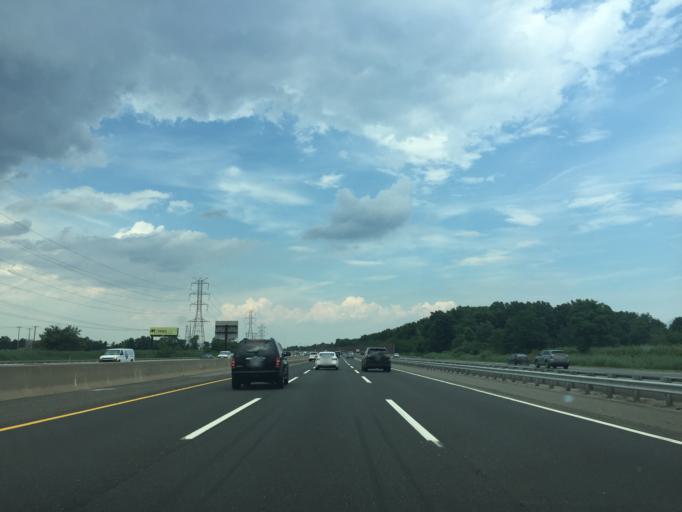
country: US
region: New Jersey
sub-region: Middlesex County
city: Port Reading
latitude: 40.5732
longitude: -74.2498
